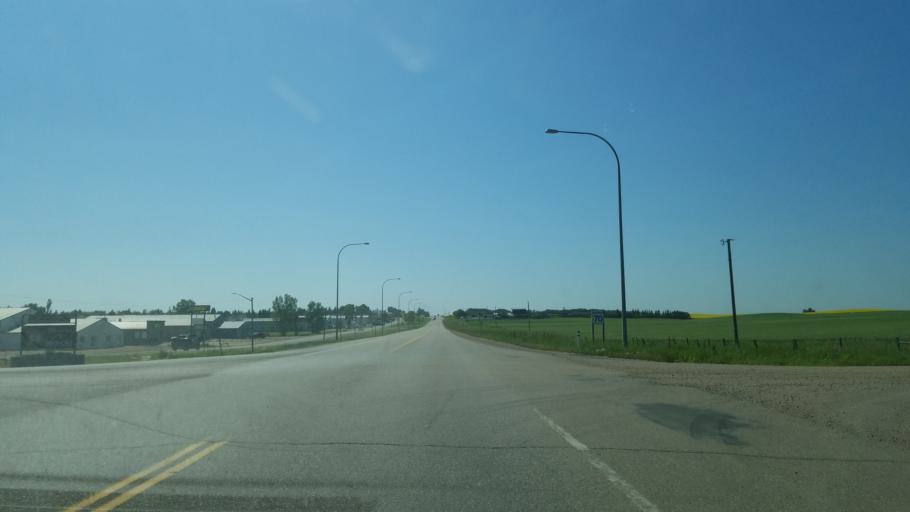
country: CA
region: Alberta
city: Provost
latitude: 52.3612
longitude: -110.2446
